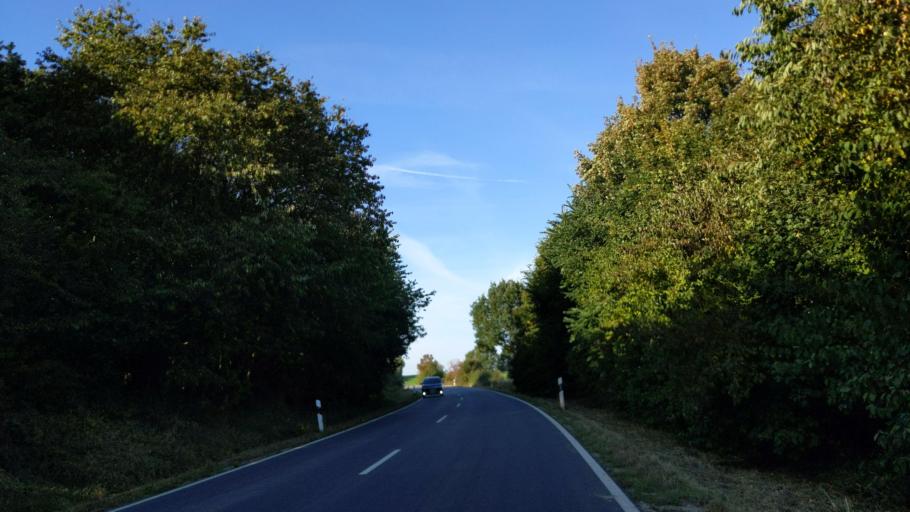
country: DE
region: Schleswig-Holstein
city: Eutin
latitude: 54.0748
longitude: 10.5917
